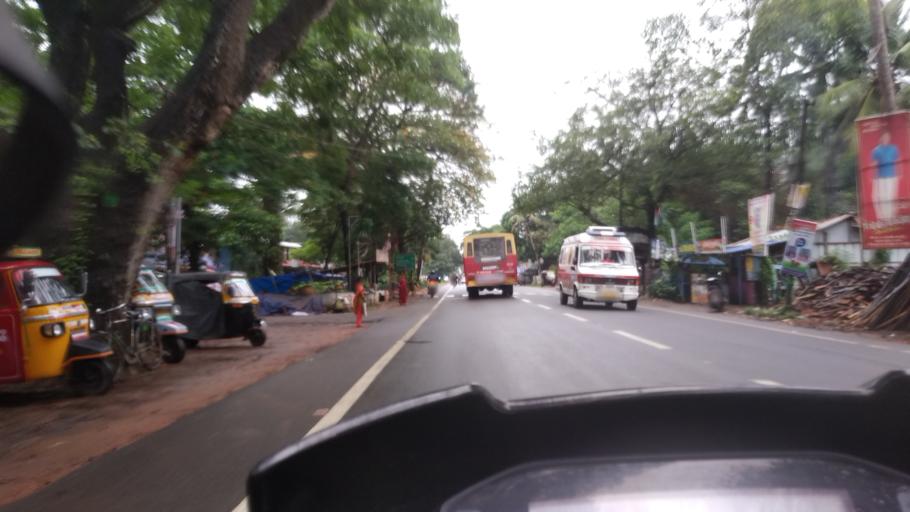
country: IN
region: Kerala
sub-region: Alappuzha
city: Mavelikara
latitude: 9.2890
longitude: 76.4376
